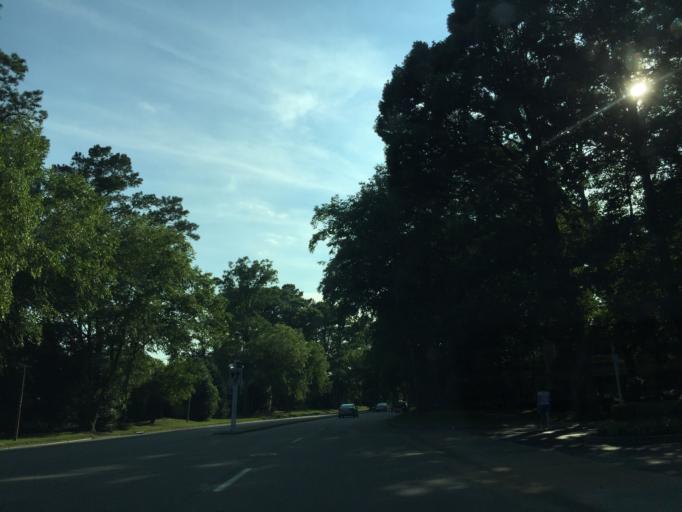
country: US
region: Virginia
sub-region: York County
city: Yorktown
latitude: 37.1162
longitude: -76.4896
